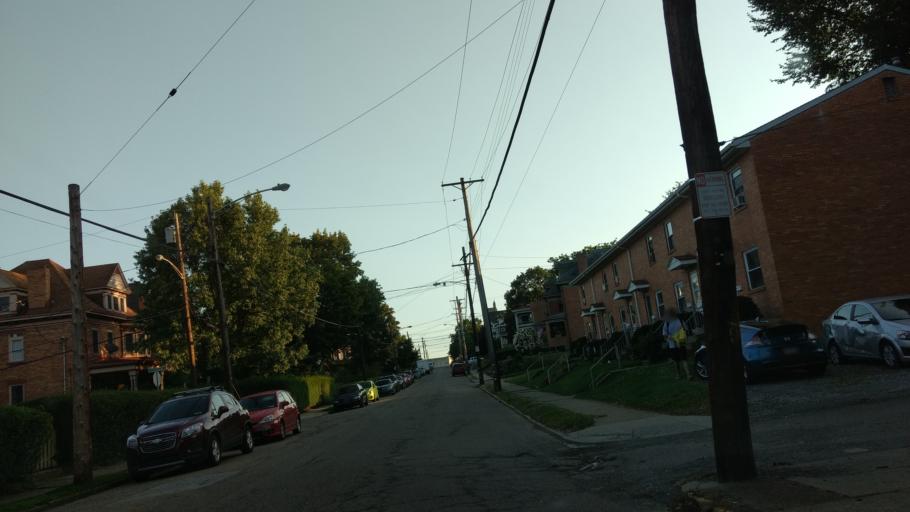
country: US
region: Pennsylvania
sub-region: Allegheny County
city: Bellevue
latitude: 40.4974
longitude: -80.0509
